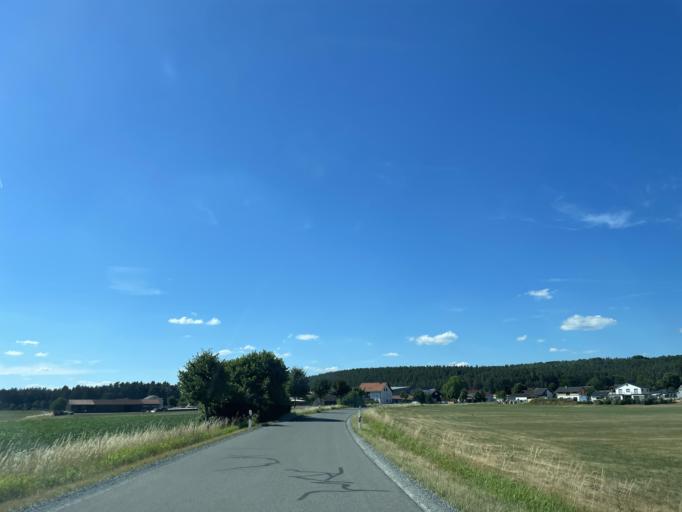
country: DE
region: Bavaria
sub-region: Upper Palatinate
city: Speinshart
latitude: 49.7712
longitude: 11.8616
